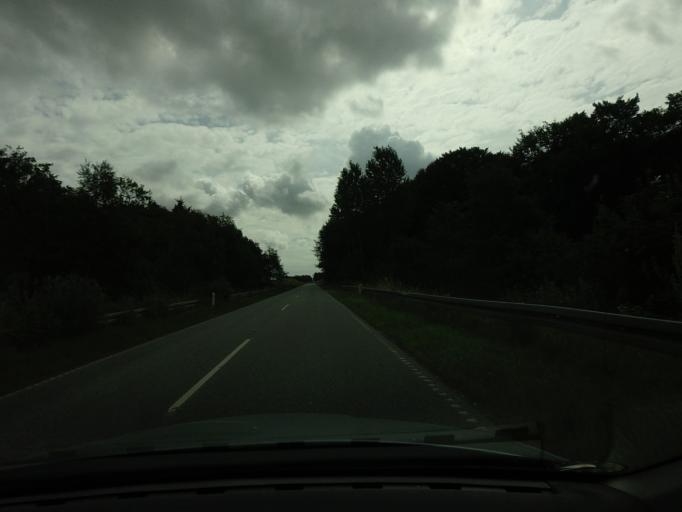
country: DK
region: North Denmark
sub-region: Bronderslev Kommune
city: Dronninglund
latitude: 57.2863
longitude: 10.3231
